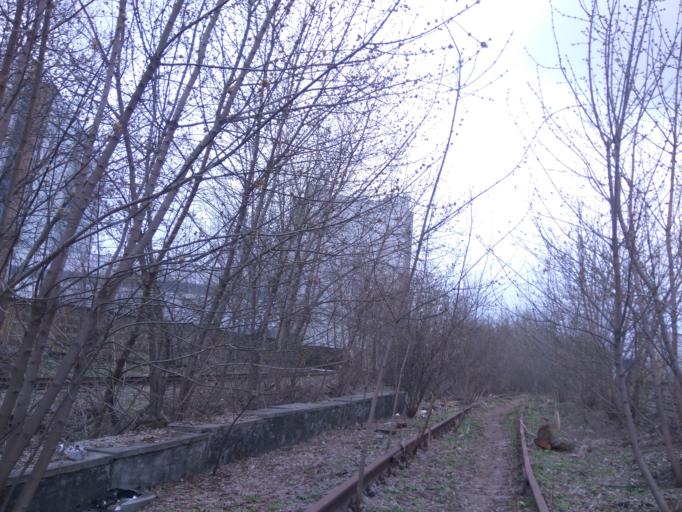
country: RU
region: Moscow
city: Vagonoremont
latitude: 55.9040
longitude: 37.5471
